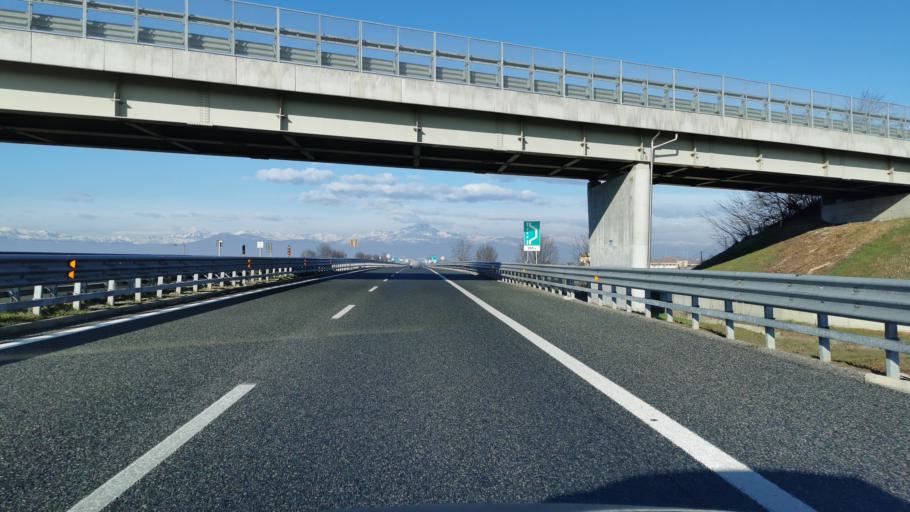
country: IT
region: Piedmont
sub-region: Provincia di Cuneo
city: Sant'Albano Stura
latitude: 44.4713
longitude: 7.7091
